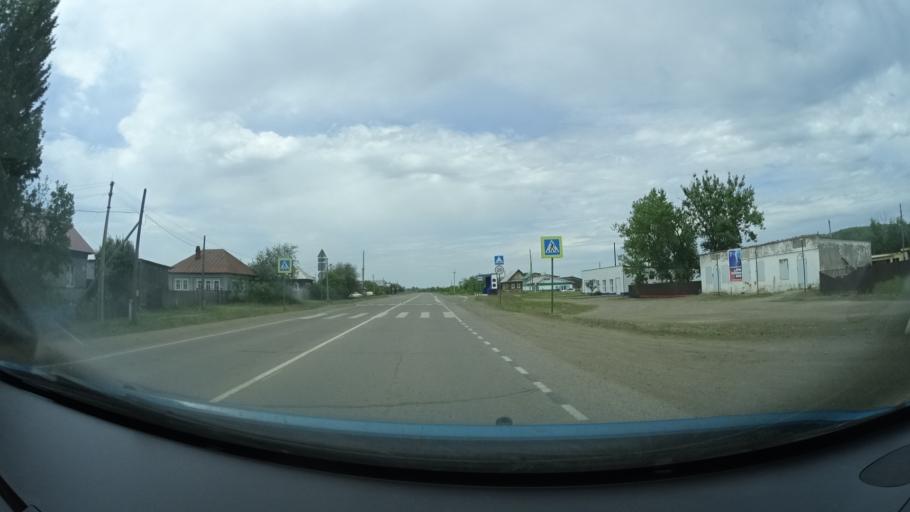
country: RU
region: Perm
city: Barda
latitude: 56.8271
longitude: 55.6269
